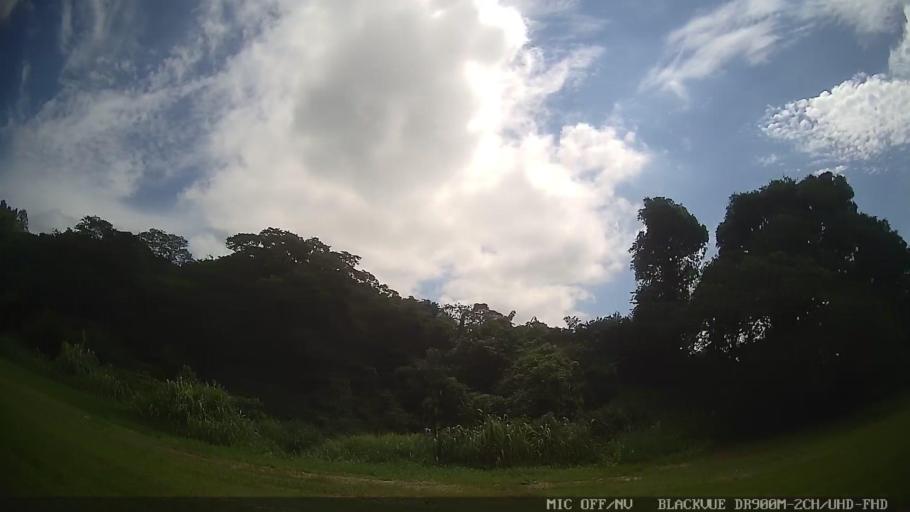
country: BR
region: Sao Paulo
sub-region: Tiete
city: Tiete
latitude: -23.1071
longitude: -47.7597
